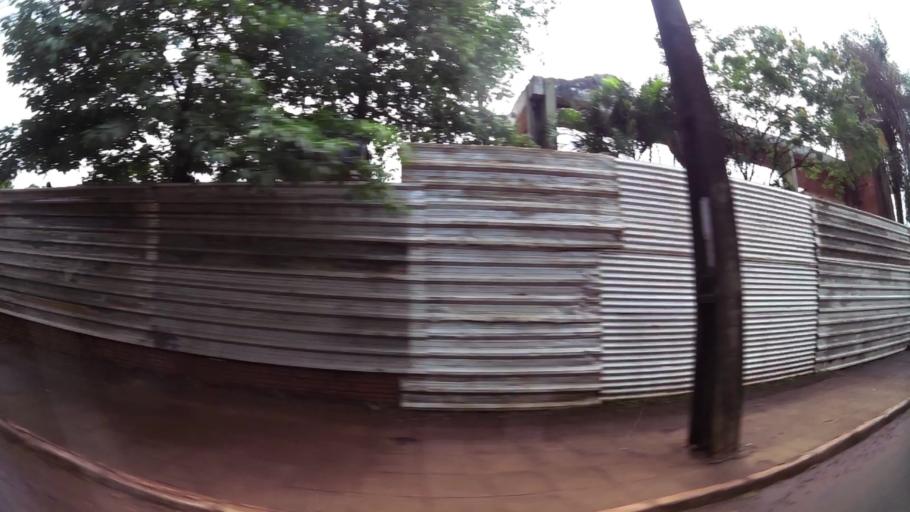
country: PY
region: Alto Parana
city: Ciudad del Este
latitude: -25.5078
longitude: -54.6665
